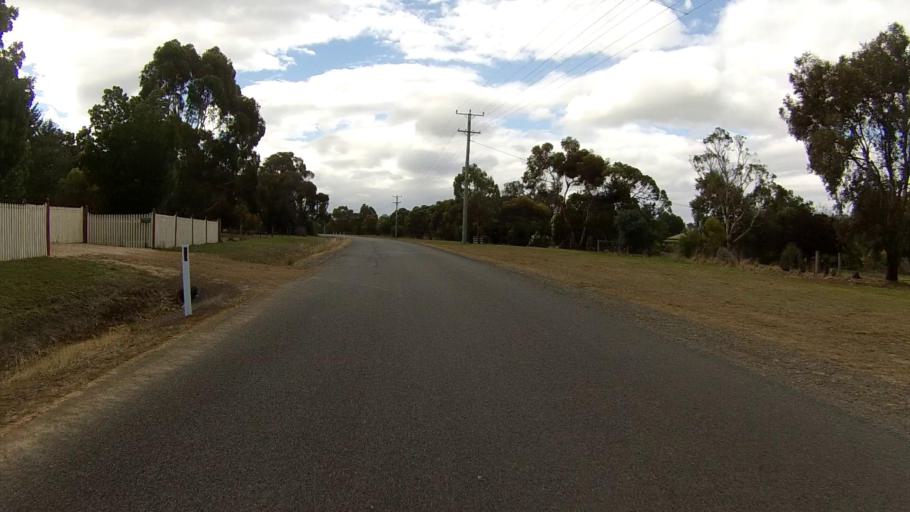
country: AU
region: Tasmania
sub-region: Clarence
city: Acton Park
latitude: -42.8622
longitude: 147.4865
